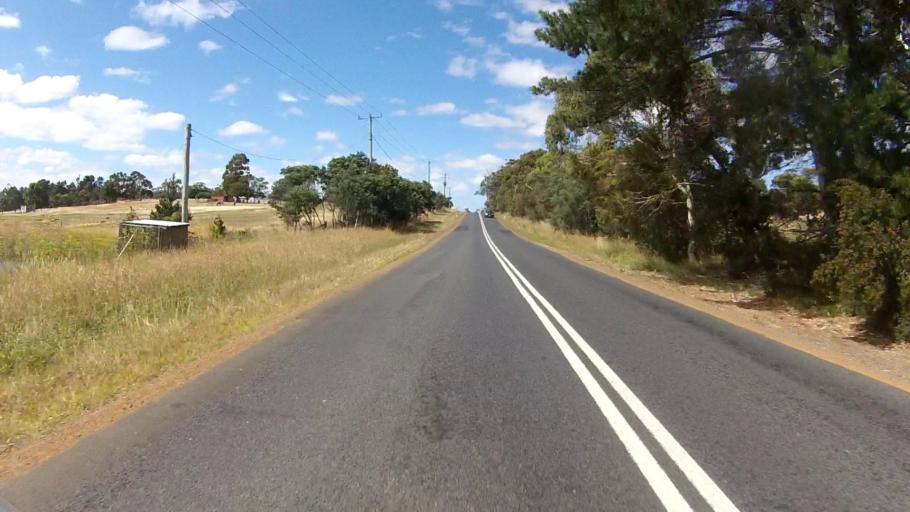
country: AU
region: Tasmania
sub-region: Sorell
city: Sorell
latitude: -42.6154
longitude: 147.4285
